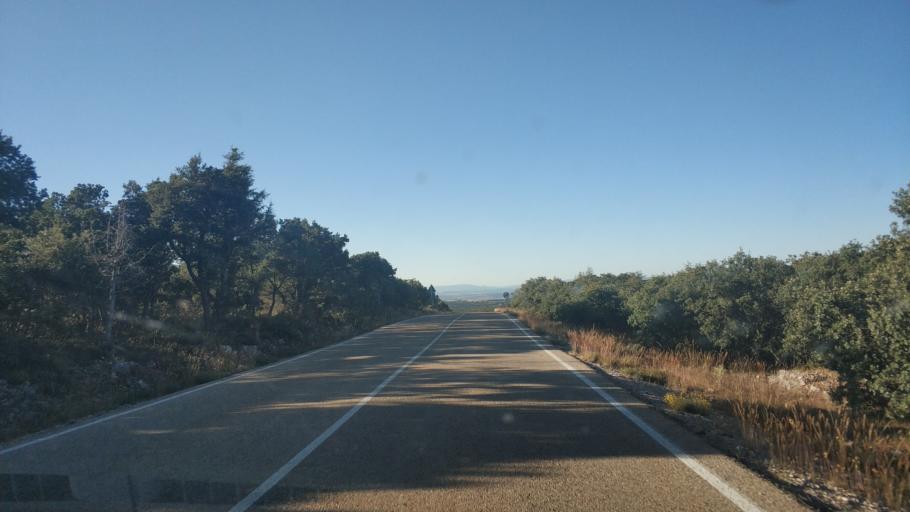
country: ES
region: Castille and Leon
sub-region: Provincia de Soria
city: Montejo de Tiermes
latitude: 41.4051
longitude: -3.2026
